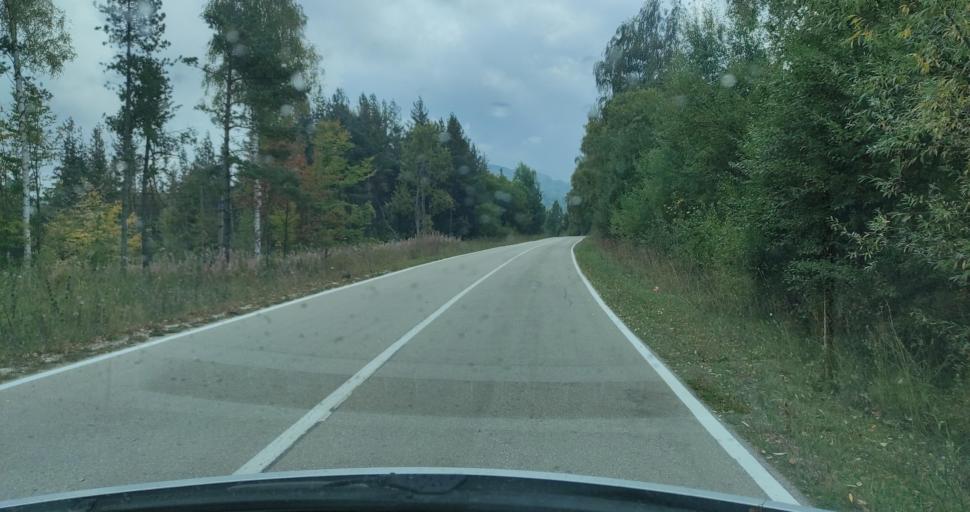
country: RS
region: Central Serbia
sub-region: Jablanicki Okrug
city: Crna Trava
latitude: 42.6746
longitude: 22.3146
